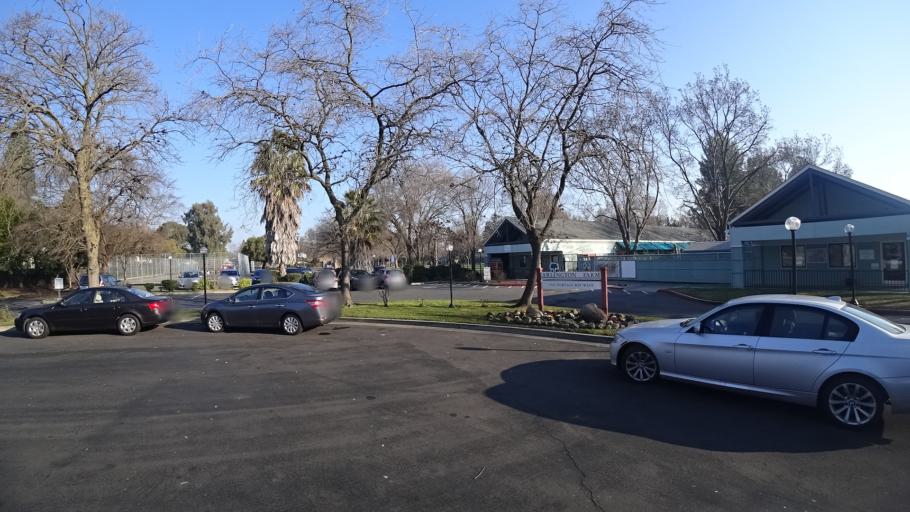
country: US
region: California
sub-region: Yolo County
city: Davis
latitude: 38.5487
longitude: -121.7862
